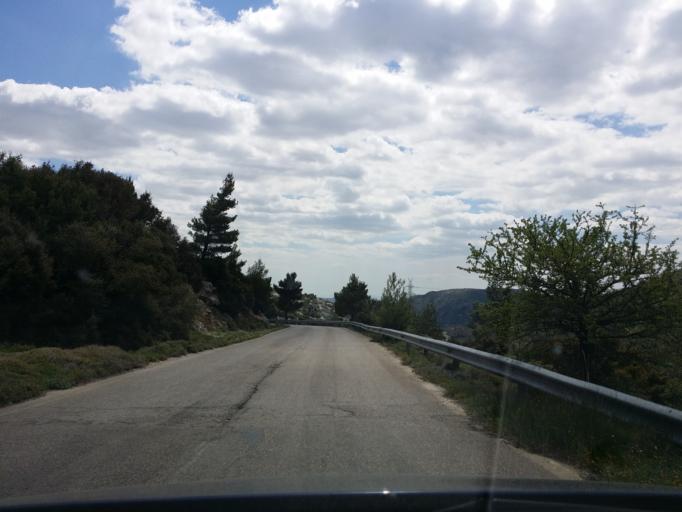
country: GR
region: Attica
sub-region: Nomarchia Dytikis Attikis
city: Fyli
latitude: 38.1434
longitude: 23.6452
